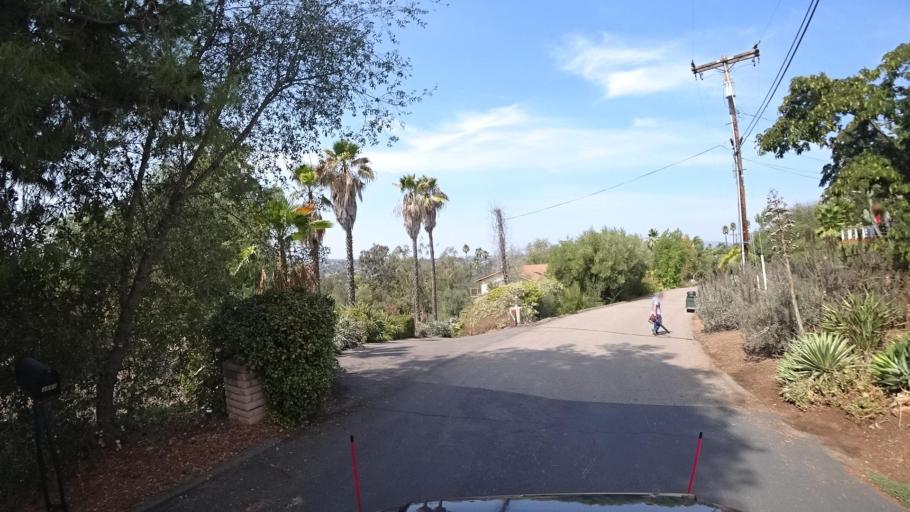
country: US
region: California
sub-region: San Diego County
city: Escondido
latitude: 33.0830
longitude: -117.0482
